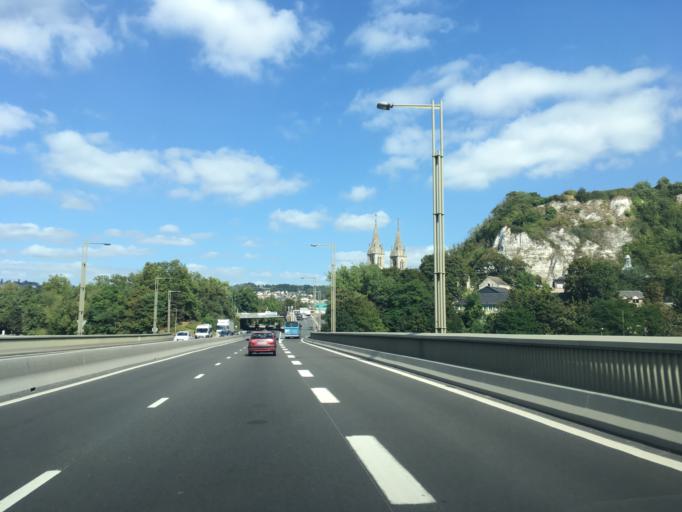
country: FR
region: Haute-Normandie
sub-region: Departement de la Seine-Maritime
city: Rouen
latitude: 49.4326
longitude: 1.1041
